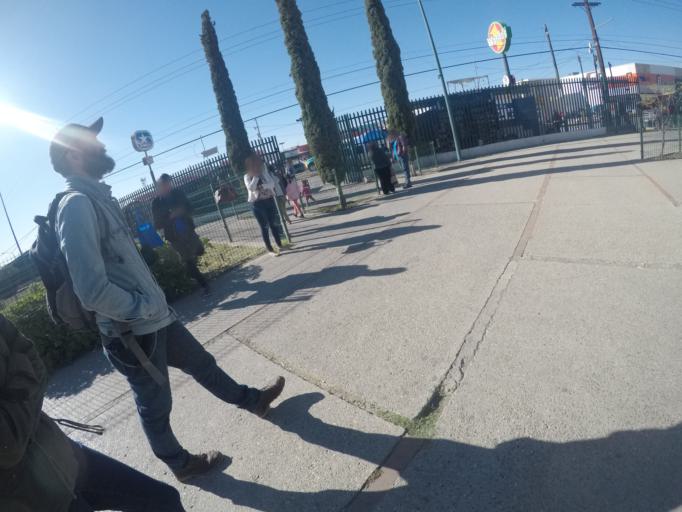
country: US
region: Texas
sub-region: El Paso County
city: Socorro
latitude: 31.6672
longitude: -106.4038
